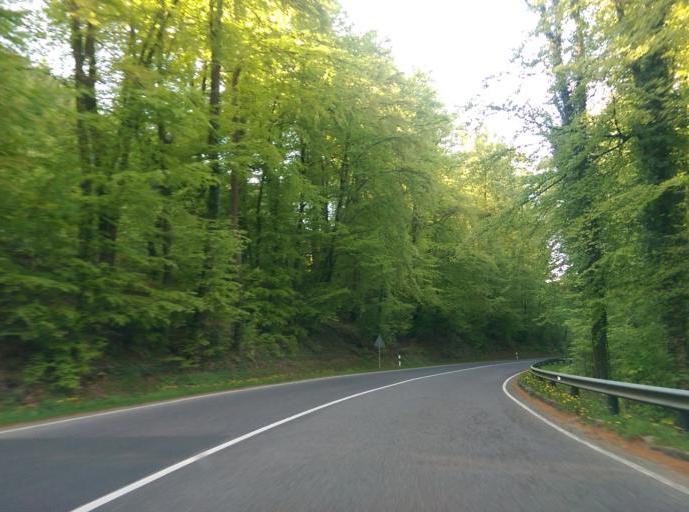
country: LU
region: Luxembourg
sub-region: Canton de Luxembourg
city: Niederanven
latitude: 49.6428
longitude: 6.2341
